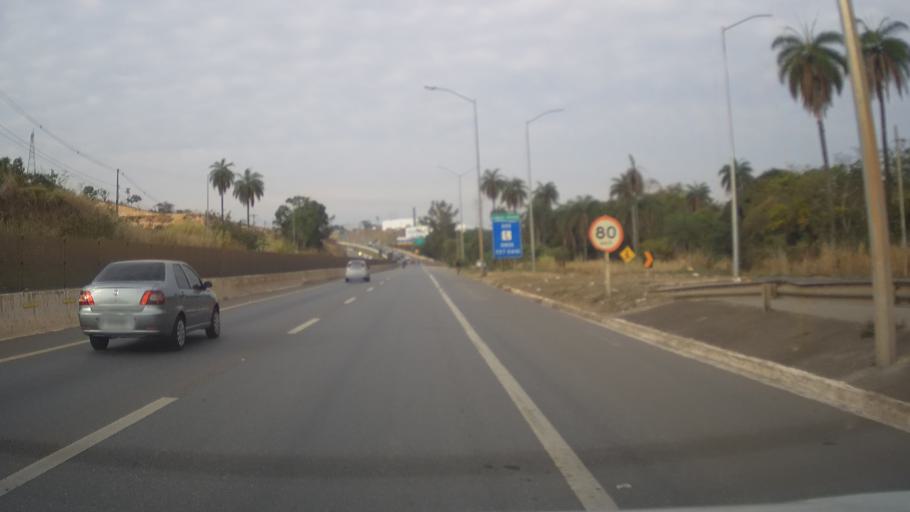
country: BR
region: Minas Gerais
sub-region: Vespasiano
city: Vespasiano
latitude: -19.7289
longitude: -43.9401
